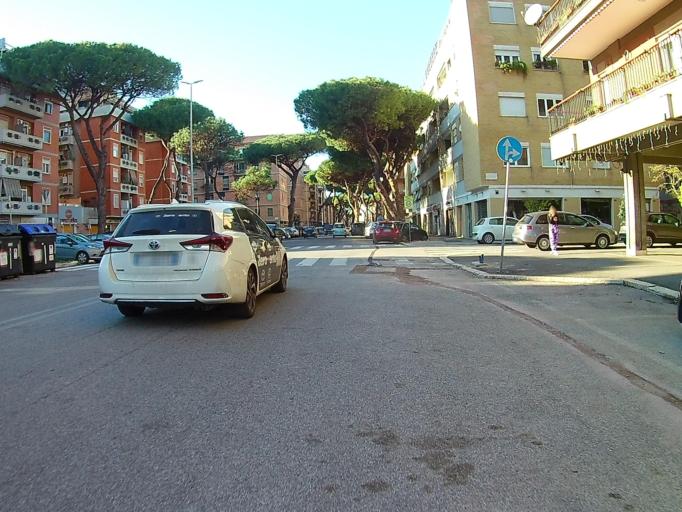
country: IT
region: Latium
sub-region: Citta metropolitana di Roma Capitale
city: Lido di Ostia
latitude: 41.7363
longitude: 12.2914
